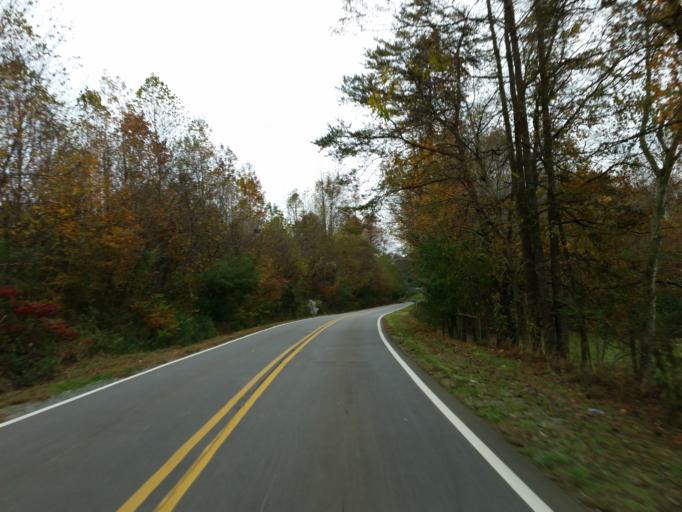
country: US
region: Georgia
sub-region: Gilmer County
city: Ellijay
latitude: 34.6610
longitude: -84.3764
